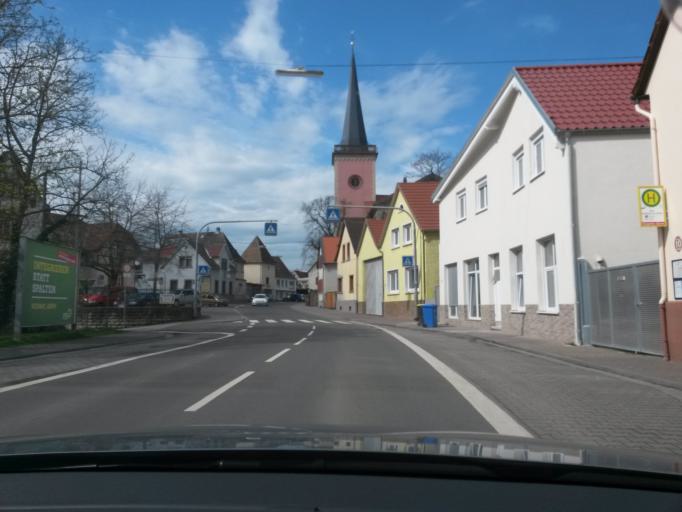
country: DE
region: Rheinland-Pfalz
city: Eich
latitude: 49.7496
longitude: 8.4072
